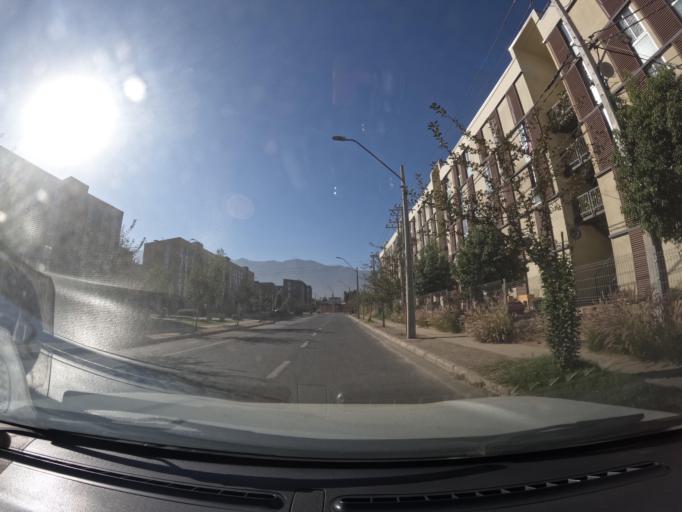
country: CL
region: Santiago Metropolitan
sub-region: Provincia de Santiago
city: Villa Presidente Frei, Nunoa, Santiago, Chile
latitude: -33.4999
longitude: -70.5842
